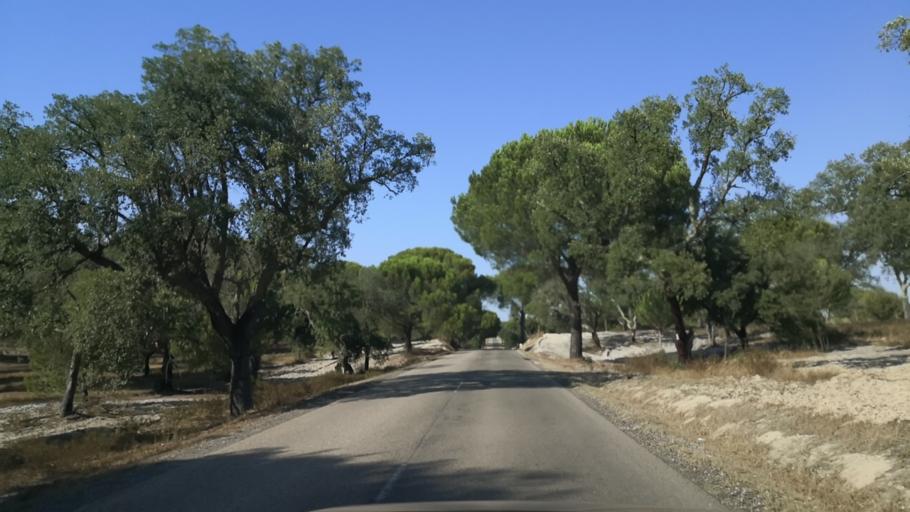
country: PT
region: Santarem
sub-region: Coruche
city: Coruche
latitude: 38.8387
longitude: -8.5571
